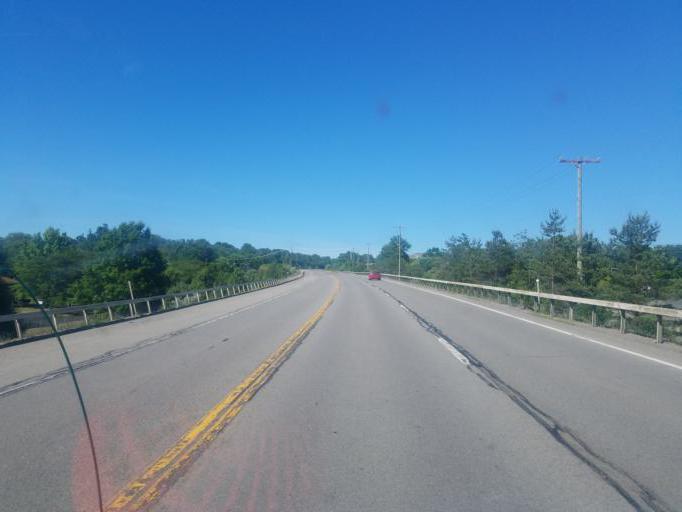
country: US
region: New York
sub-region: Ontario County
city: Canandaigua
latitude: 42.8766
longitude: -77.2815
